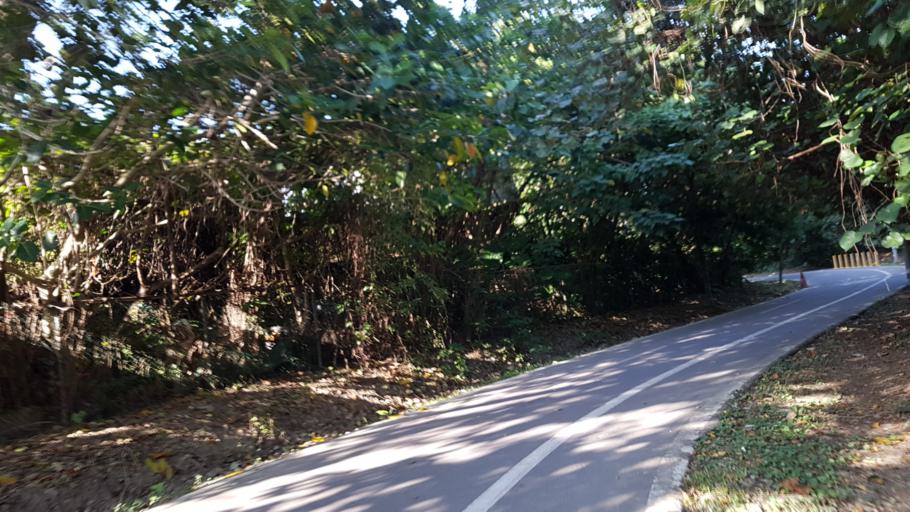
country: TW
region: Taipei
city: Taipei
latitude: 25.0053
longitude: 121.5300
